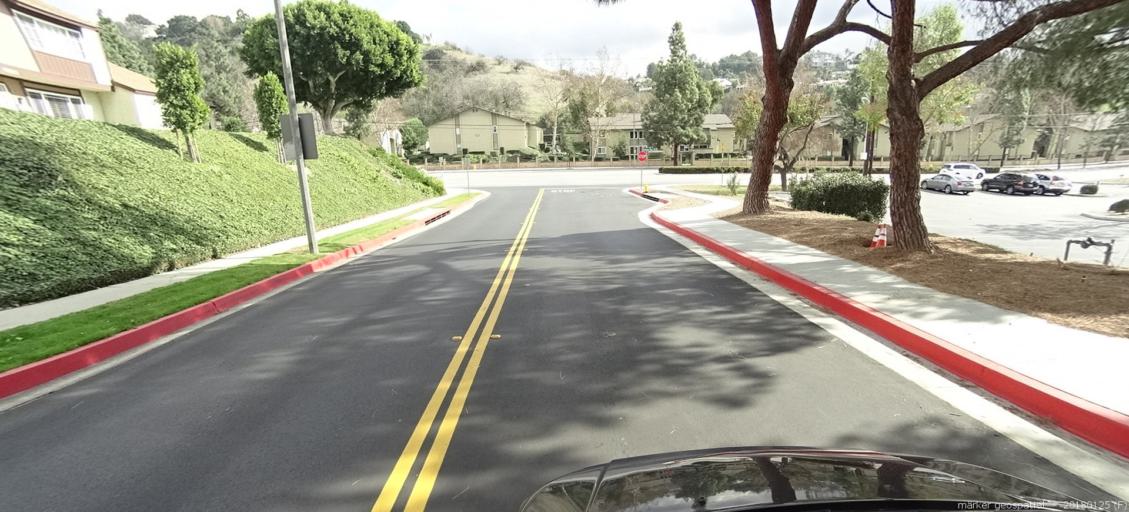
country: US
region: California
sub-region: Los Angeles County
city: Diamond Bar
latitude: 33.9832
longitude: -117.8301
